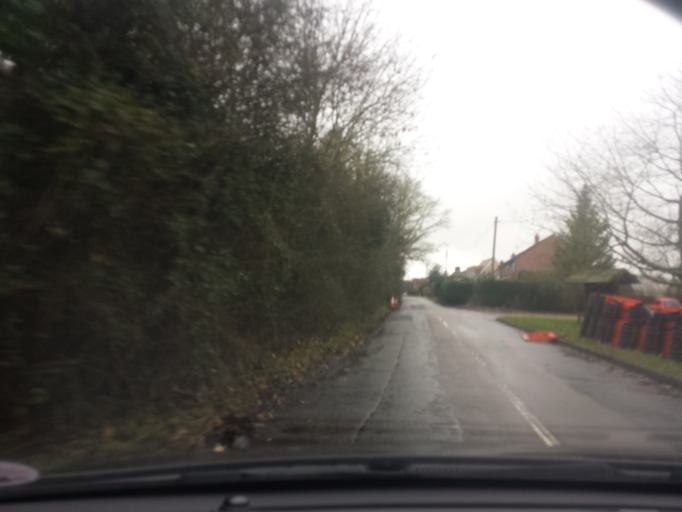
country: GB
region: England
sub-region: Essex
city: Great Bentley
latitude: 51.8902
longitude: 1.0751
